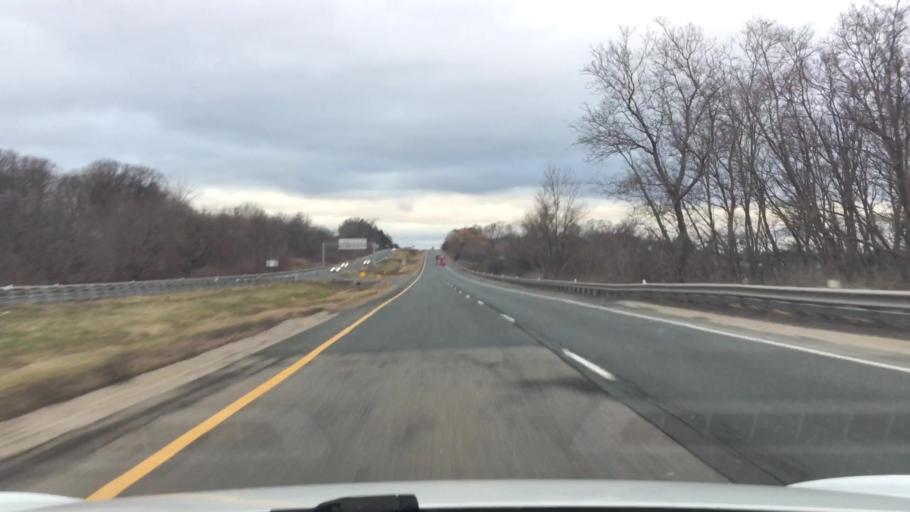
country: CA
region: Ontario
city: Niagara Falls
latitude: 43.1469
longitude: -79.1018
